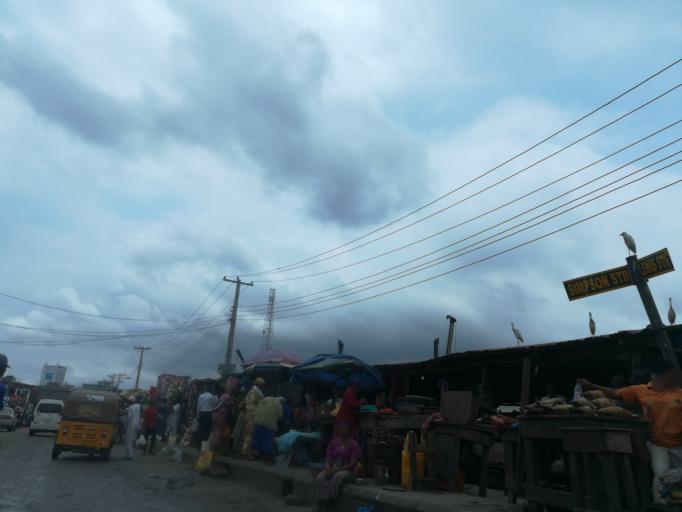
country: NG
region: Lagos
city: Lagos
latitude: 6.4511
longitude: 3.4018
